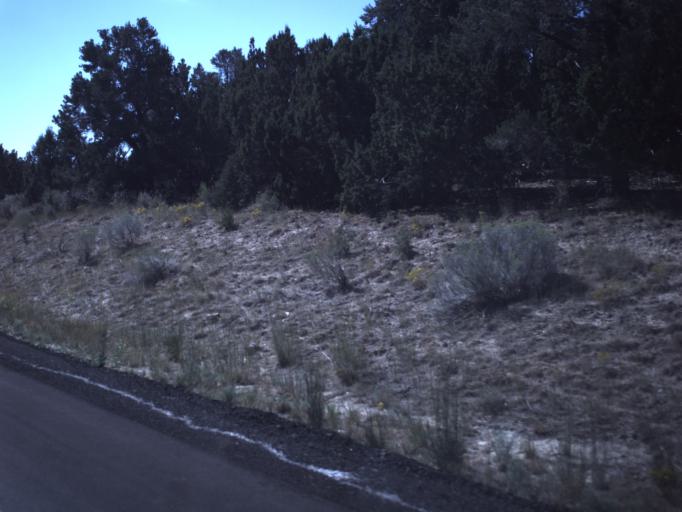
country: US
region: Utah
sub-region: Utah County
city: Genola
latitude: 39.9580
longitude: -112.2441
